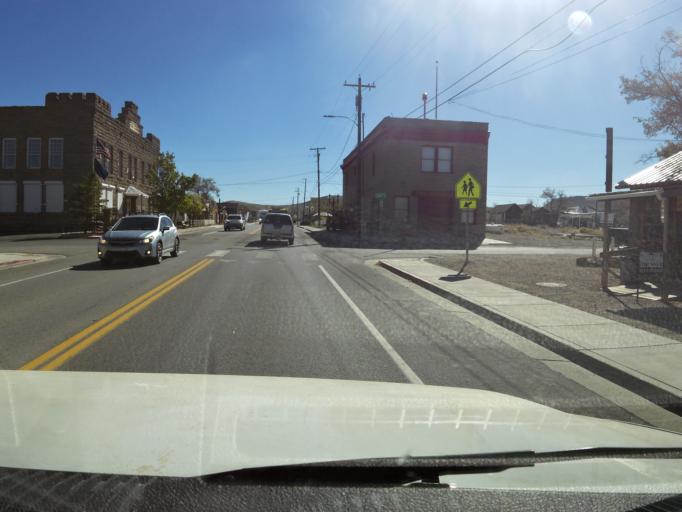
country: US
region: Nevada
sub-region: Esmeralda County
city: Goldfield
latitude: 37.7078
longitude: -117.2342
